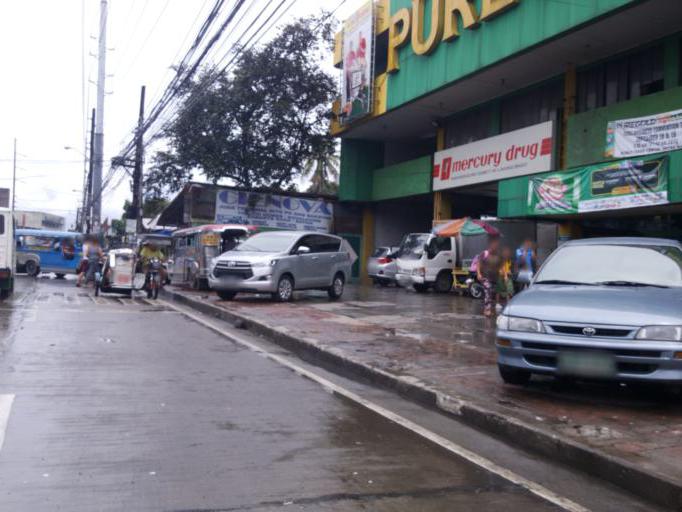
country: PH
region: Calabarzon
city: Bagong Pagasa
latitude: 14.7243
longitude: 121.0414
